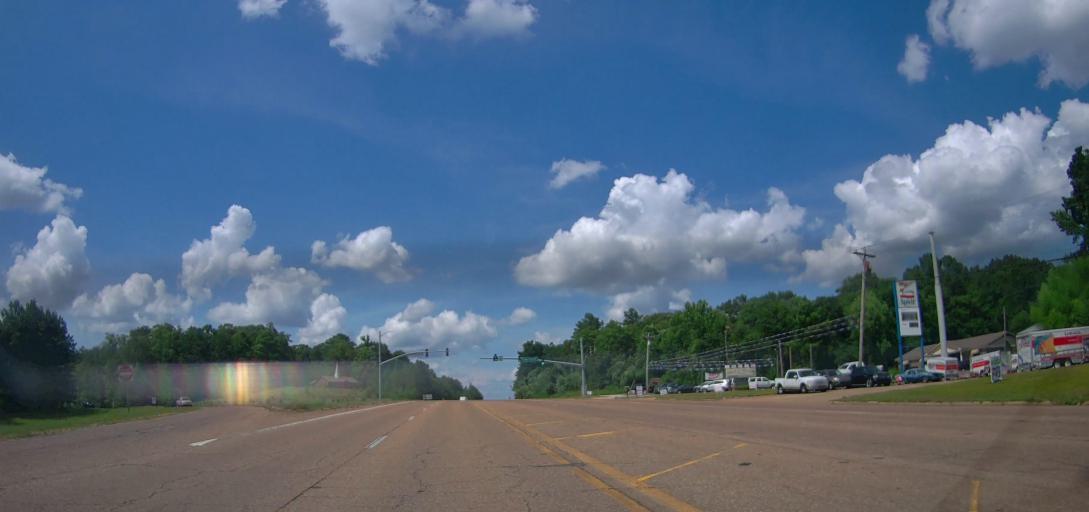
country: US
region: Mississippi
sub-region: Lowndes County
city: Columbus
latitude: 33.5621
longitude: -88.4330
